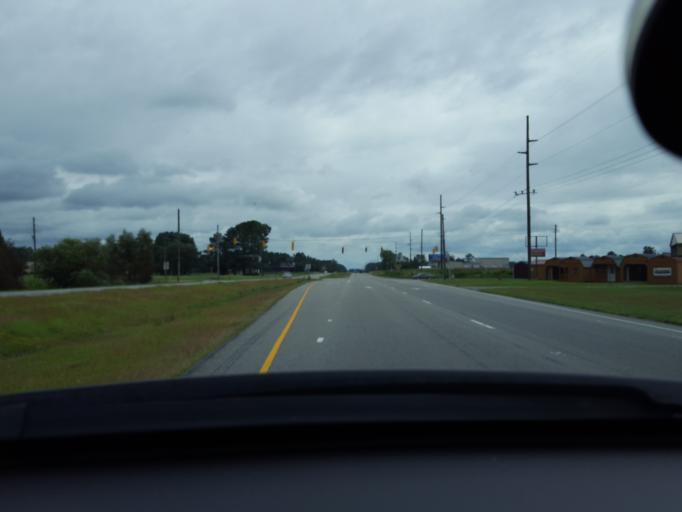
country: US
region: North Carolina
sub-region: Pitt County
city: Ayden
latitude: 35.4323
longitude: -77.4334
